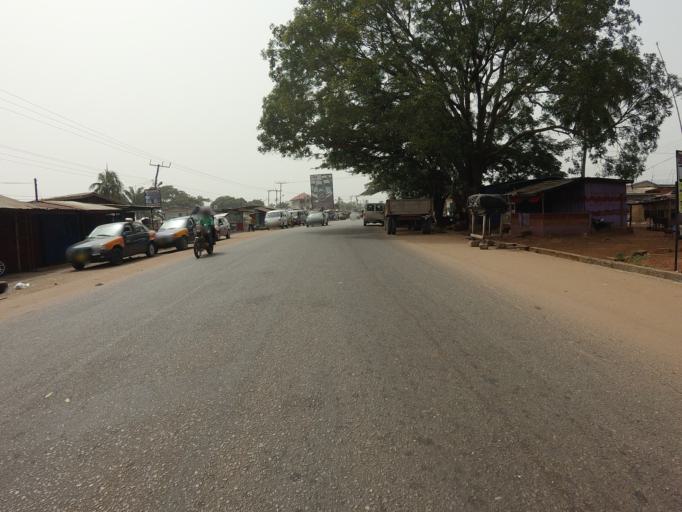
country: GH
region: Volta
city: Anloga
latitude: 5.8984
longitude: 0.5222
